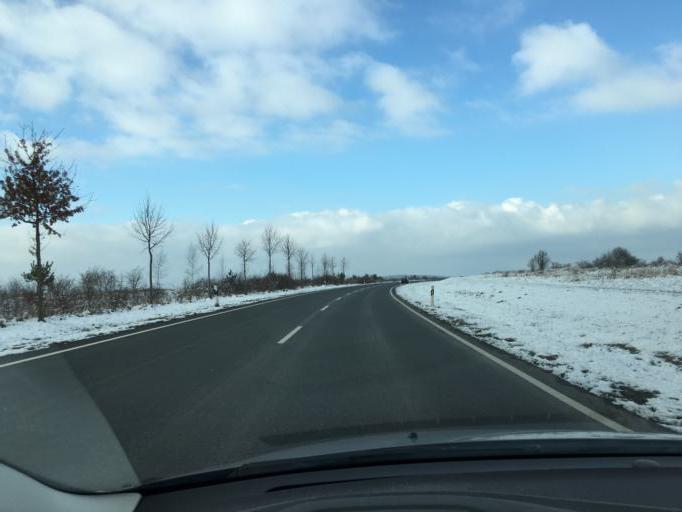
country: DE
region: Saxony
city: Grossbardau
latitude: 51.2251
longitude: 12.6997
